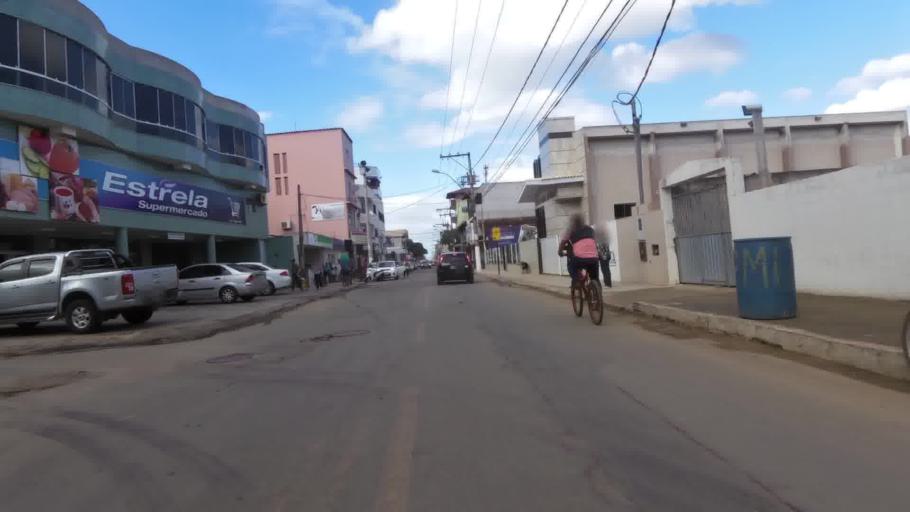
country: BR
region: Espirito Santo
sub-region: Piuma
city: Piuma
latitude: -20.8891
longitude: -40.7743
